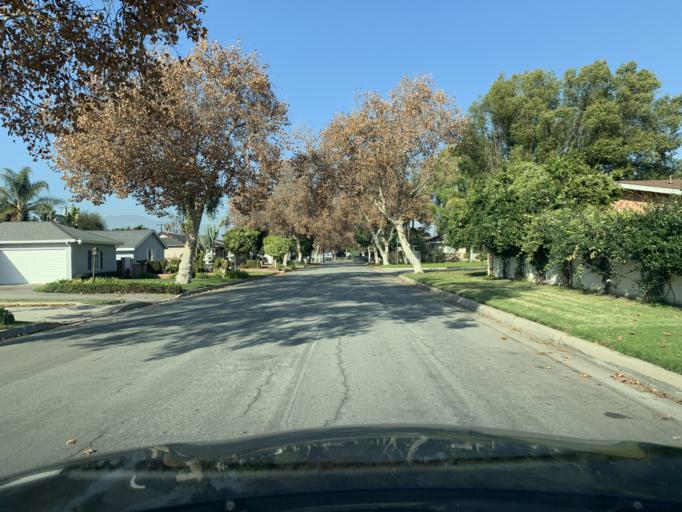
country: US
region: California
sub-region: Los Angeles County
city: Covina
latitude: 34.0758
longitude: -117.9006
